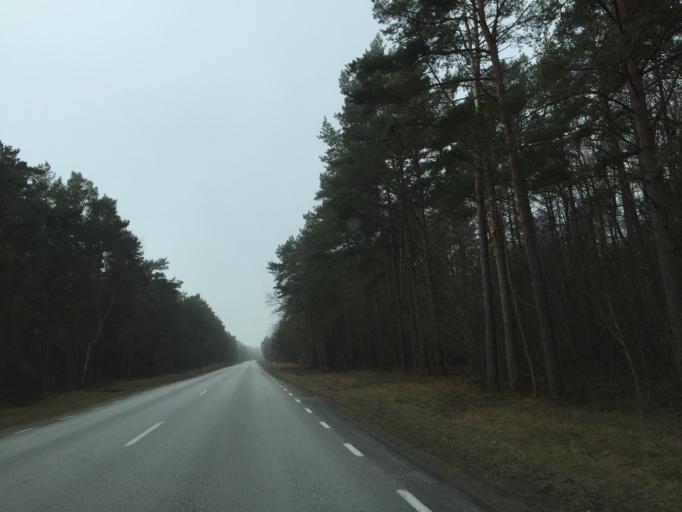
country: EE
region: Saare
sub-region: Kuressaare linn
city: Kuressaare
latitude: 58.2010
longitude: 22.2881
